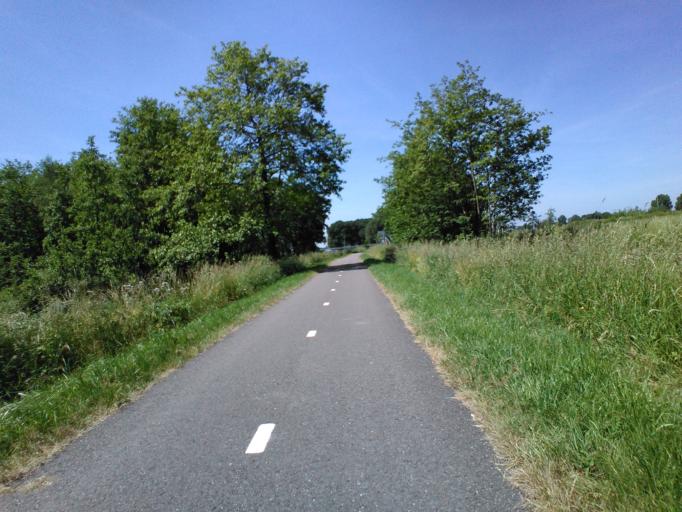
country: NL
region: South Holland
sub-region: Molenwaard
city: Nieuw-Lekkerland
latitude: 51.9170
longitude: 4.6629
